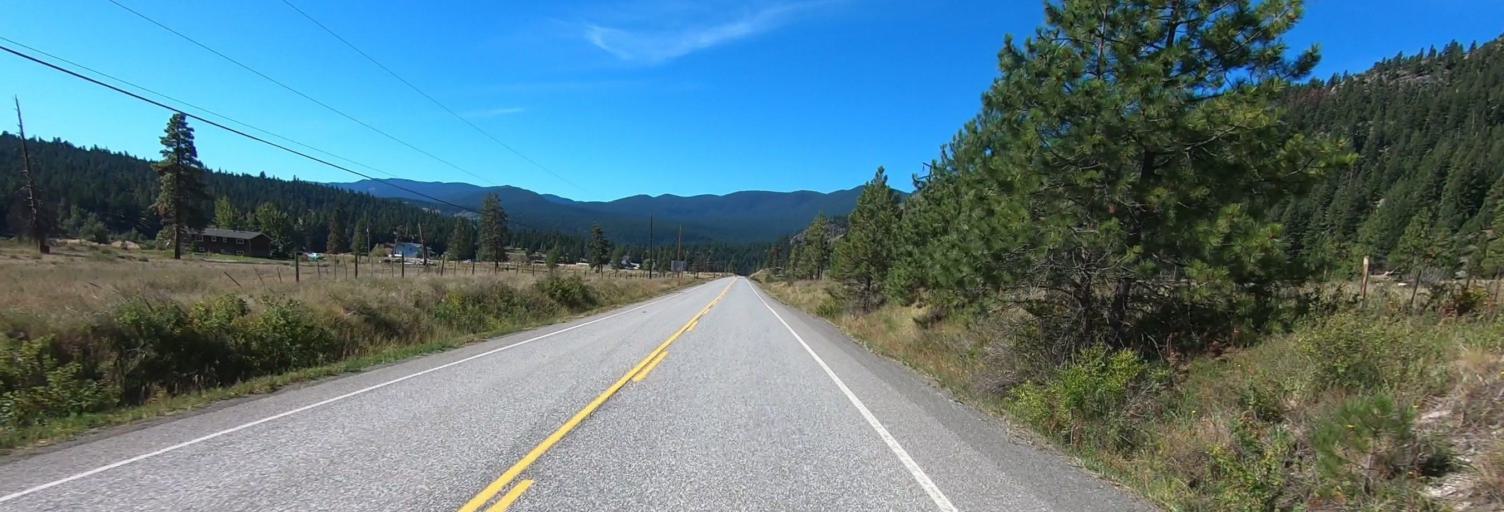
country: CA
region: British Columbia
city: Cache Creek
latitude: 50.8050
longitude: -121.5977
